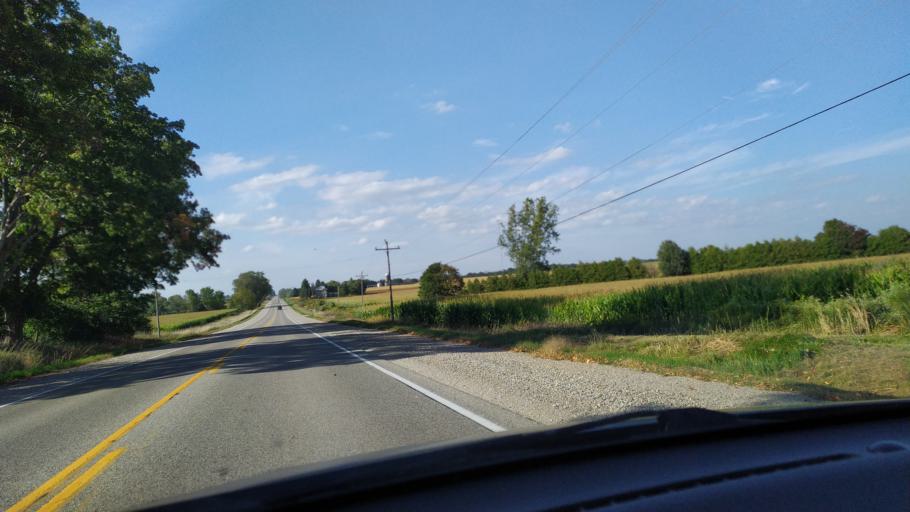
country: CA
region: Ontario
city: Ingersoll
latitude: 43.1282
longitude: -80.8873
